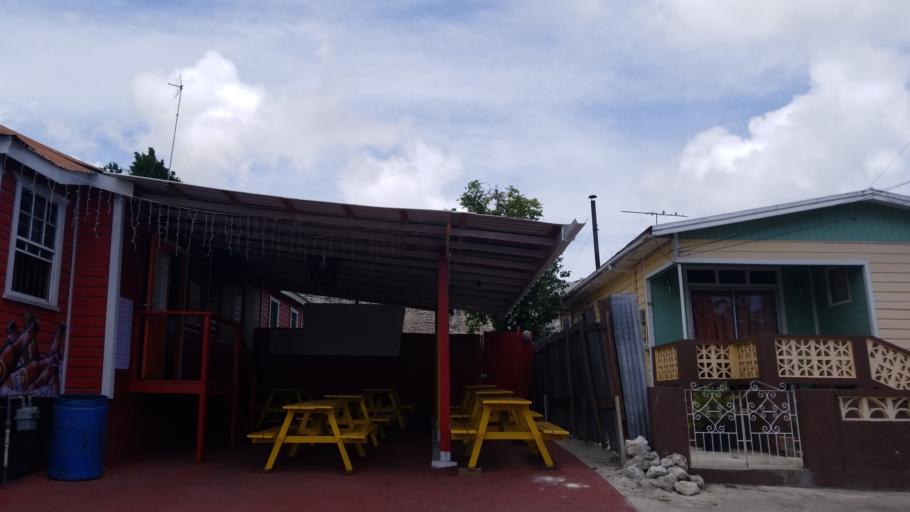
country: BB
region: Saint Michael
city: Bridgetown
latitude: 13.0883
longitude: -59.6088
